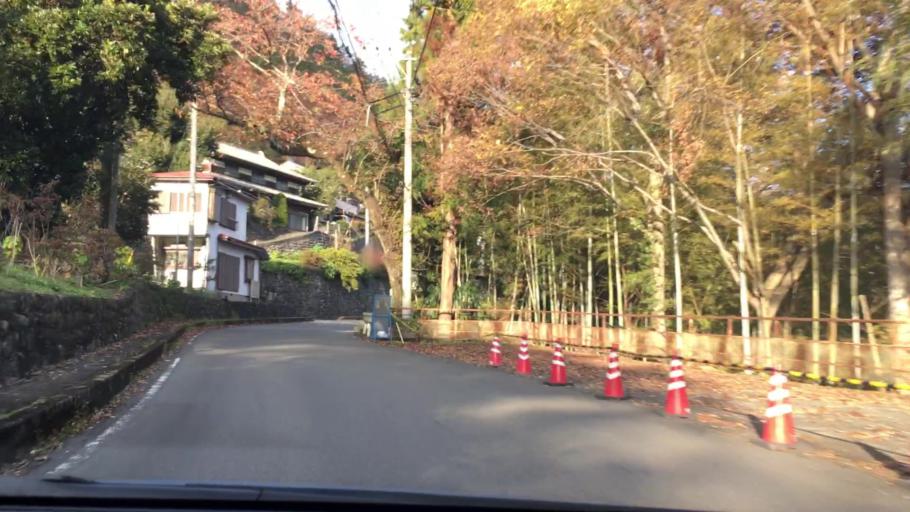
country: JP
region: Yamanashi
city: Uenohara
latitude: 35.5505
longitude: 139.1366
